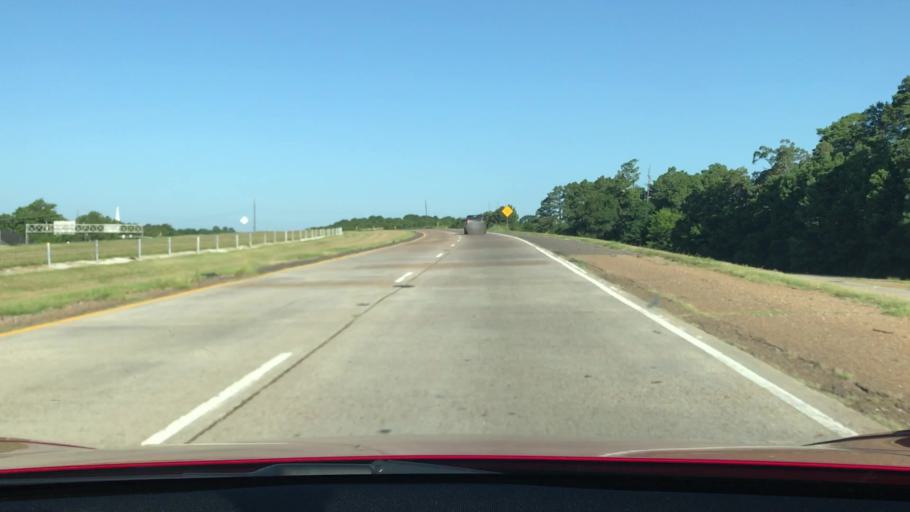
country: US
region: Louisiana
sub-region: Caddo Parish
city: Shreveport
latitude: 32.4171
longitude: -93.7940
